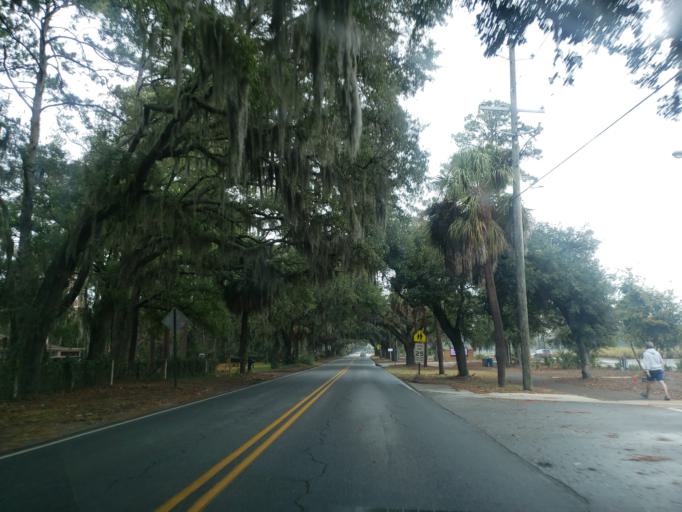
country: US
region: Georgia
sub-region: Chatham County
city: Wilmington Island
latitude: 32.0084
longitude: -80.9873
